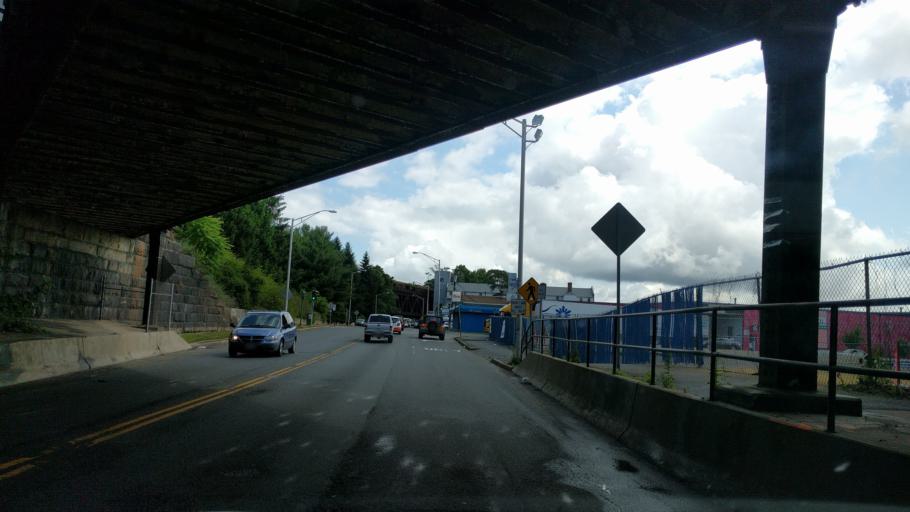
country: US
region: Massachusetts
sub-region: Worcester County
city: Worcester
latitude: 42.2523
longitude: -71.8080
